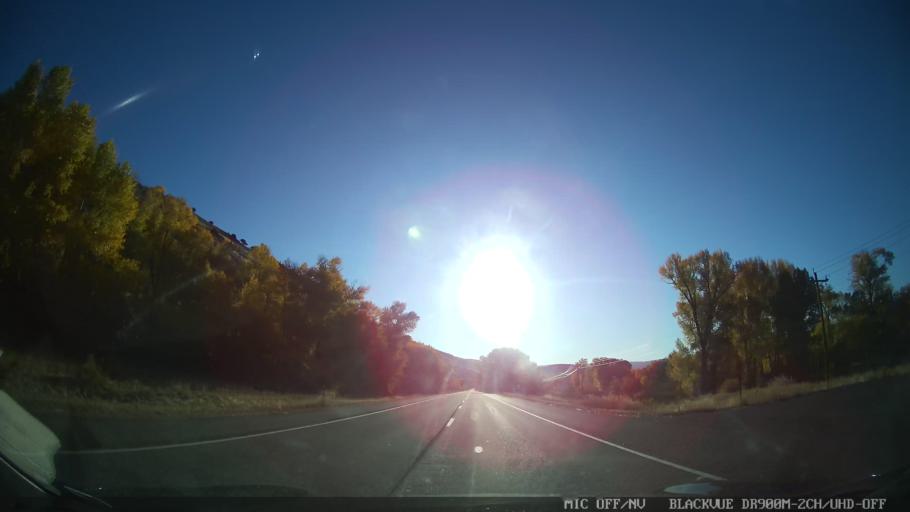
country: US
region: Colorado
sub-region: Grand County
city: Hot Sulphur Springs
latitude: 40.0653
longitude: -106.1940
